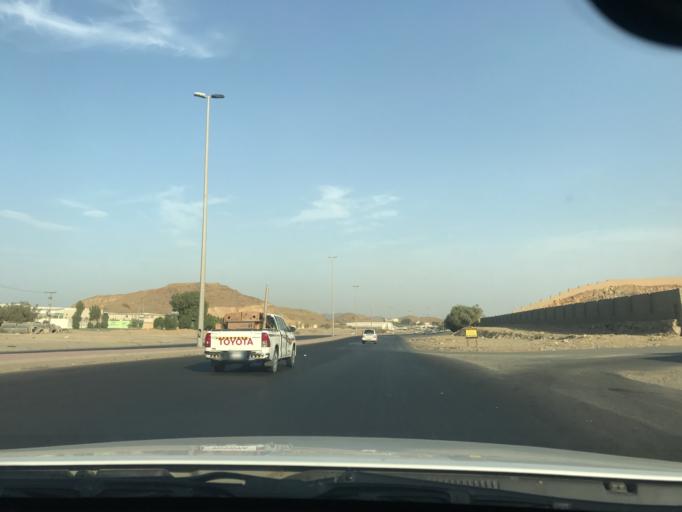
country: SA
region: Makkah
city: Jeddah
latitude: 21.4107
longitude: 39.4232
